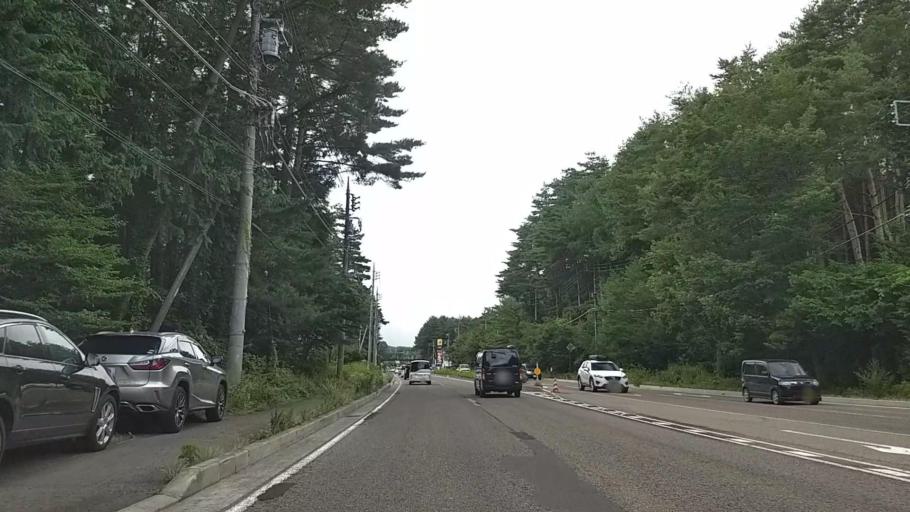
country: JP
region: Yamanashi
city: Fujikawaguchiko
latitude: 35.4868
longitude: 138.7336
